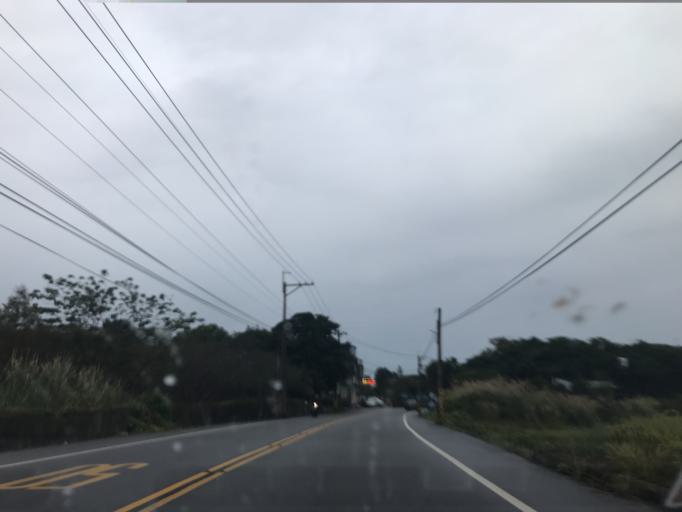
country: TW
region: Taiwan
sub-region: Hsinchu
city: Zhubei
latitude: 24.8389
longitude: 121.1084
